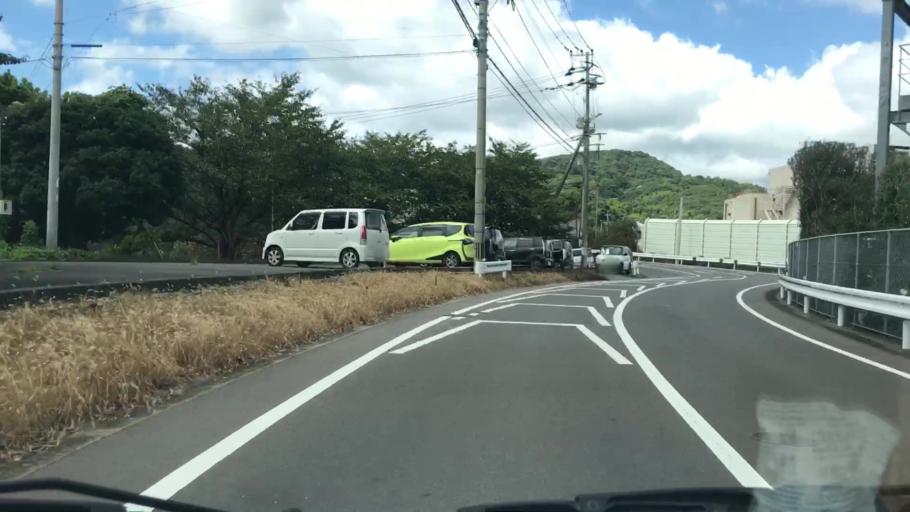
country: JP
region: Saga Prefecture
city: Takeocho-takeo
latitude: 33.2303
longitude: 130.1405
